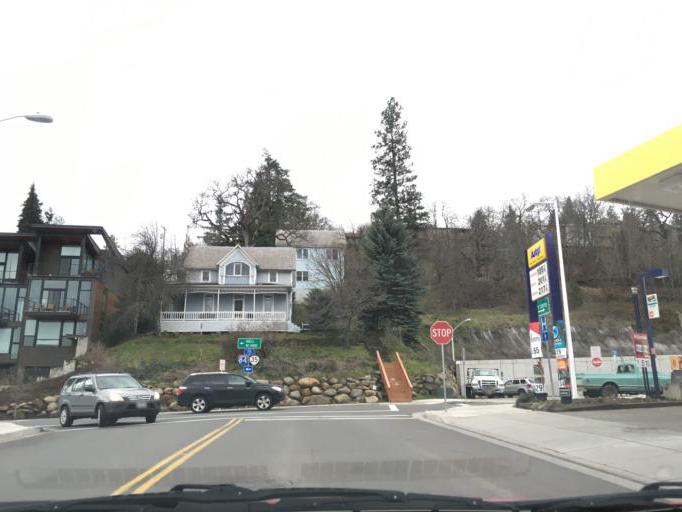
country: US
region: Oregon
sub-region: Hood River County
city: Hood River
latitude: 45.7084
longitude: -121.5102
